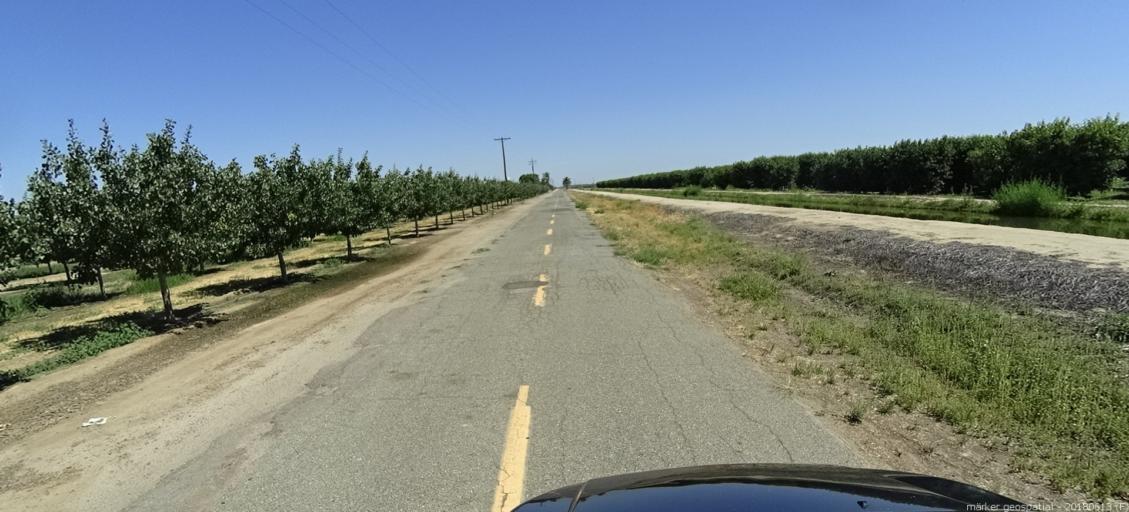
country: US
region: California
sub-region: Madera County
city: Chowchilla
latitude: 37.0580
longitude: -120.3650
